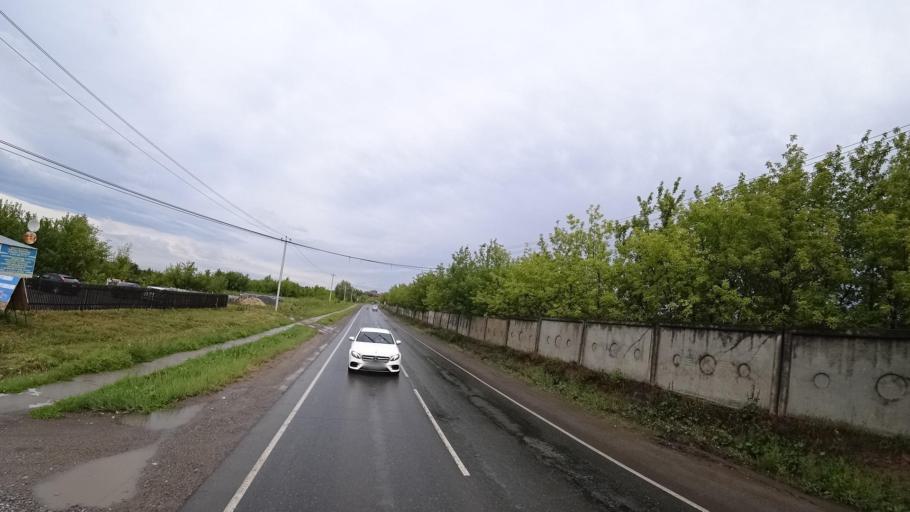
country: RU
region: Sverdlovsk
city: Kamyshlov
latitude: 56.8559
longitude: 62.7210
